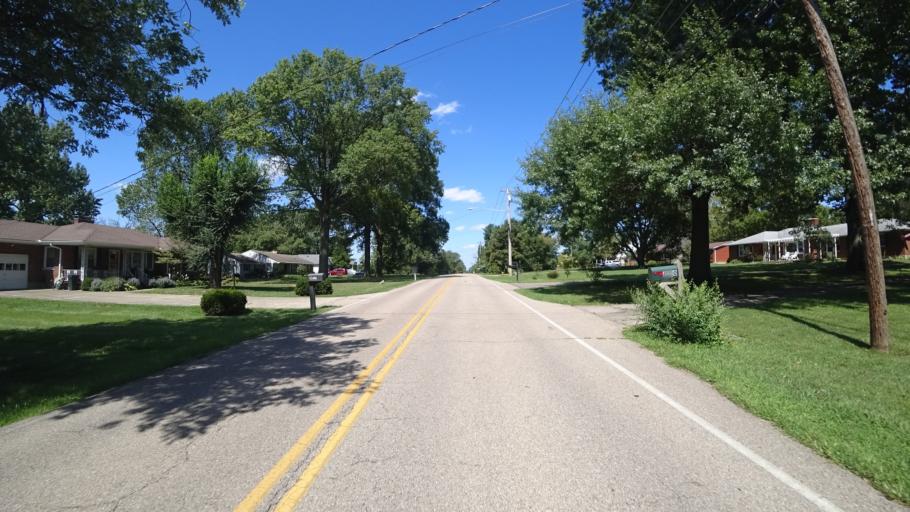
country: US
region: Ohio
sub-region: Butler County
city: New Miami
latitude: 39.4069
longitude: -84.5262
